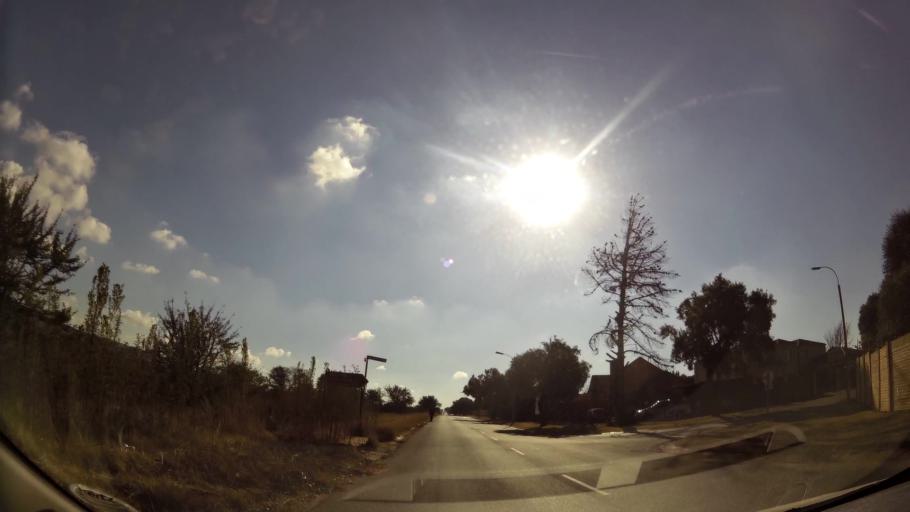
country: ZA
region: Gauteng
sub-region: City of Johannesburg Metropolitan Municipality
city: Roodepoort
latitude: -26.1630
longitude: 27.8153
